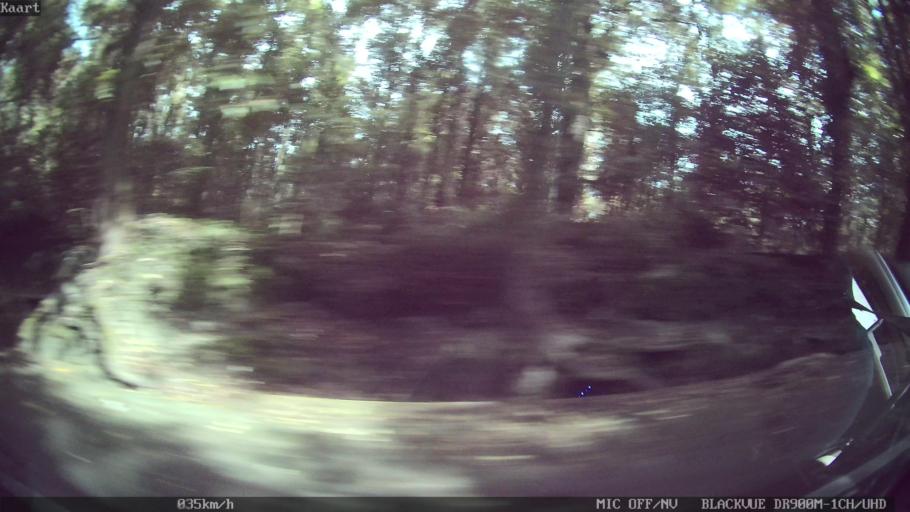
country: ID
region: Bali
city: Banjar Buahan
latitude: -8.2900
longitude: 115.3812
